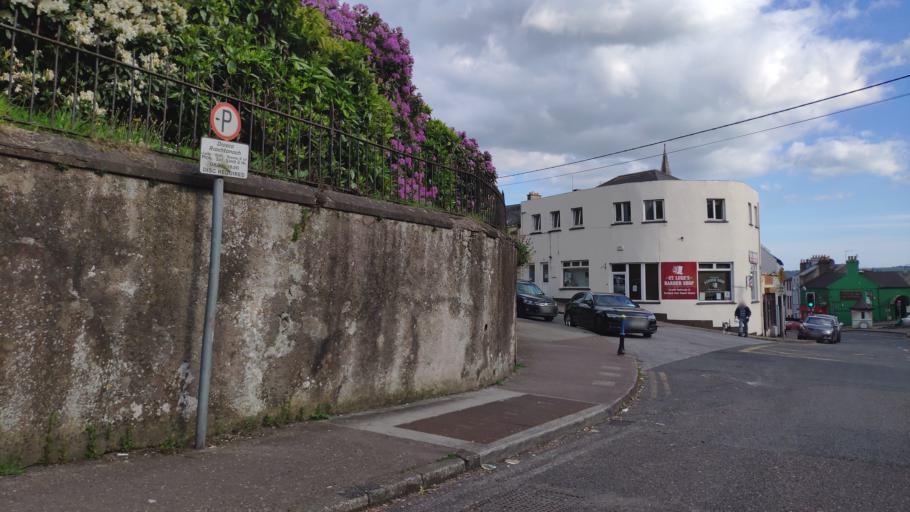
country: IE
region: Munster
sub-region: County Cork
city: Cork
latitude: 51.9055
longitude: -8.4578
